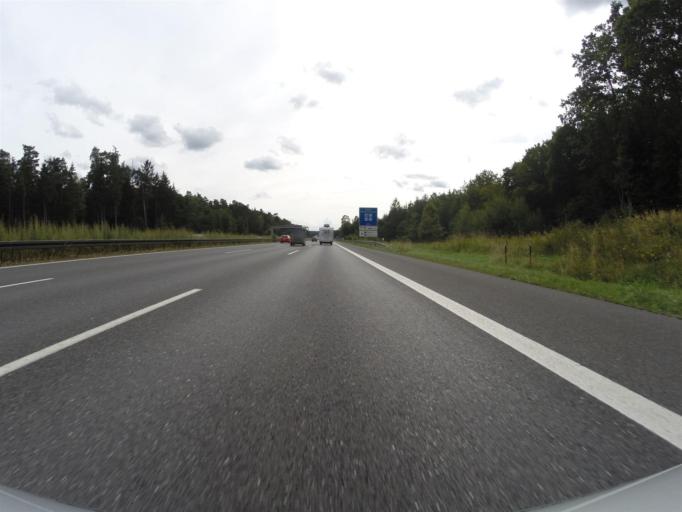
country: DE
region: Bavaria
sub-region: Regierungsbezirk Mittelfranken
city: Schwaig
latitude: 49.4307
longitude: 11.2150
